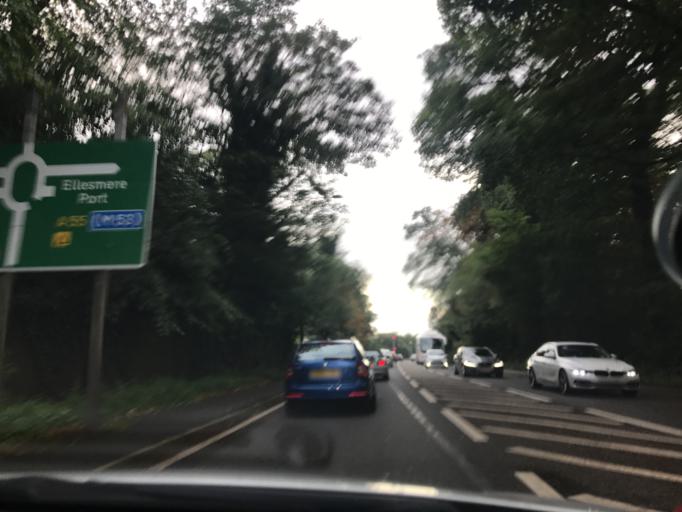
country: GB
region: England
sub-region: Cheshire West and Chester
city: Guilden Sutton
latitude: 53.1954
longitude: -2.8404
